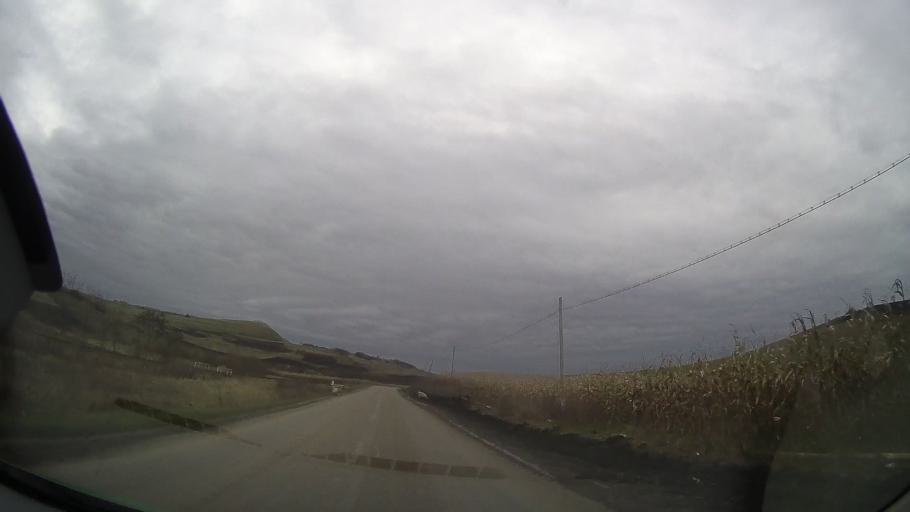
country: RO
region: Cluj
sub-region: Comuna Catina
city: Catina
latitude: 46.8140
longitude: 24.2242
